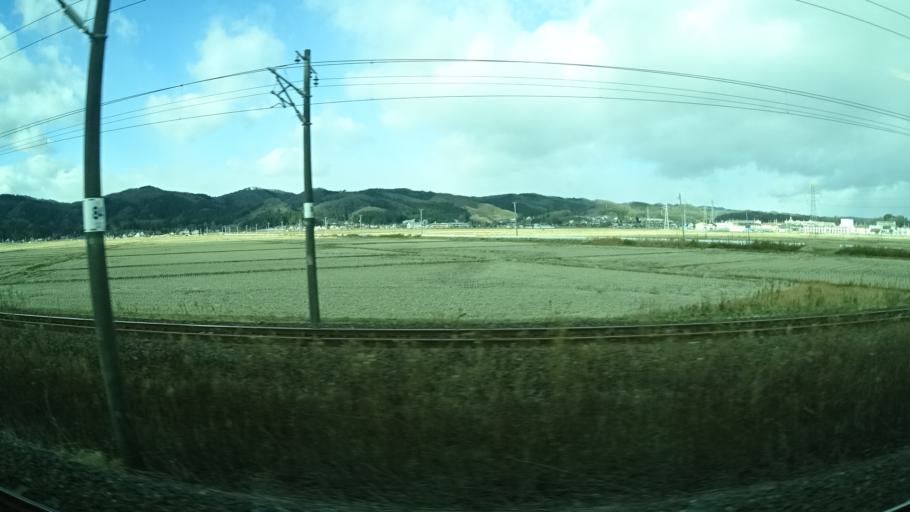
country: JP
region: Miyagi
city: Iwanuma
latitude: 38.1026
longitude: 140.8561
